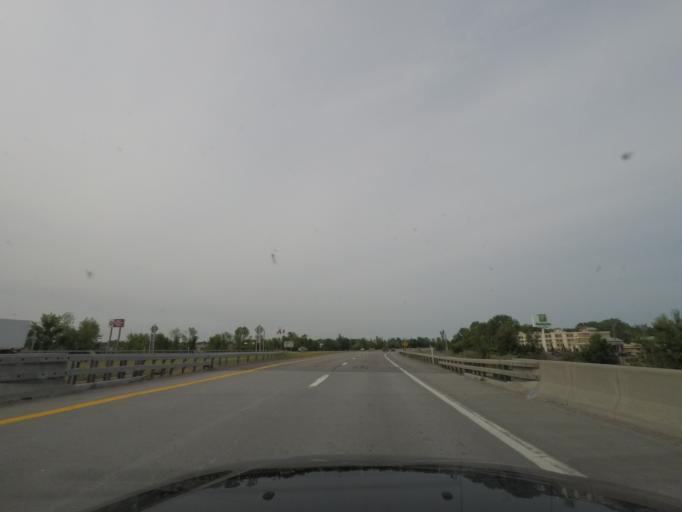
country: US
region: New York
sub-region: Clinton County
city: Plattsburgh West
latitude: 44.6967
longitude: -73.4900
